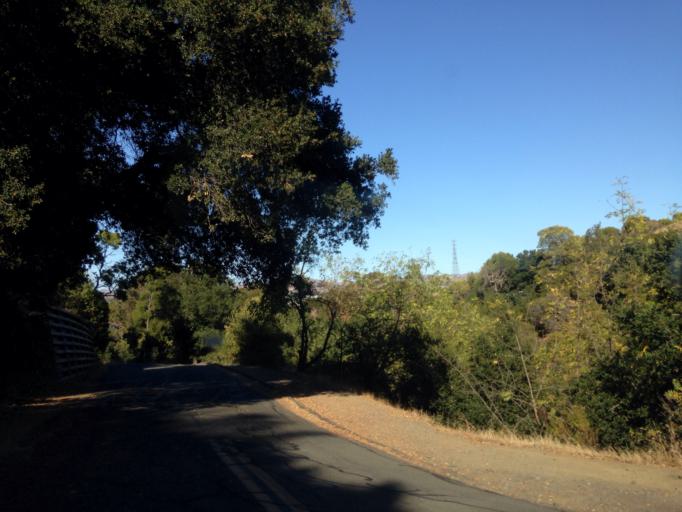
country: US
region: California
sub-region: Contra Costa County
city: Crockett
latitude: 38.0517
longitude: -122.2087
